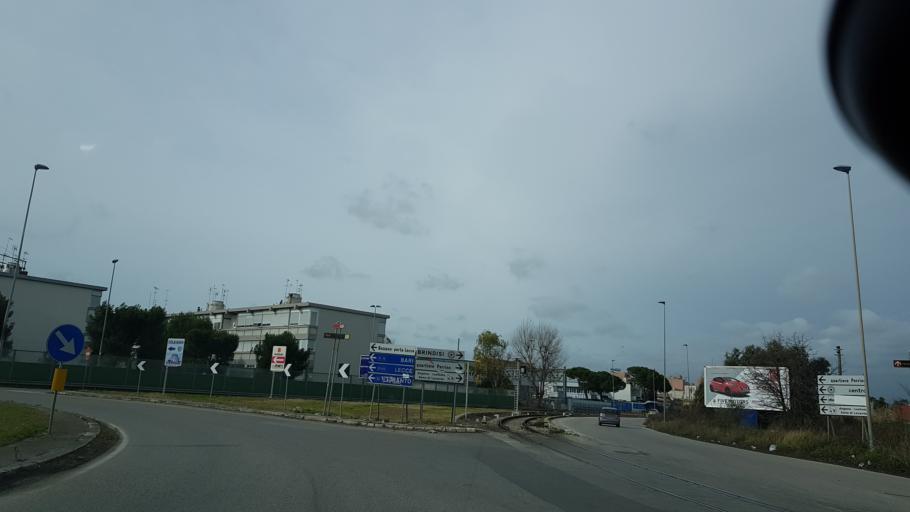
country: IT
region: Apulia
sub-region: Provincia di Brindisi
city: La Rosa
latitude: 40.6288
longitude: 17.9617
